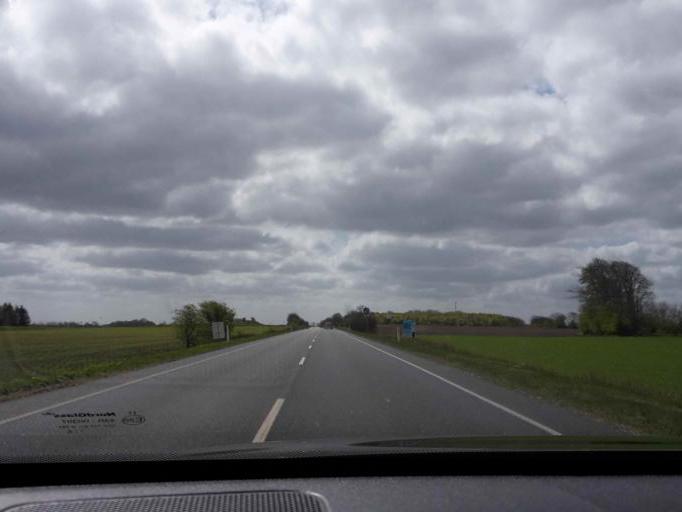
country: DK
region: South Denmark
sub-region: Varde Kommune
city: Olgod
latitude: 55.7690
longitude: 8.6218
